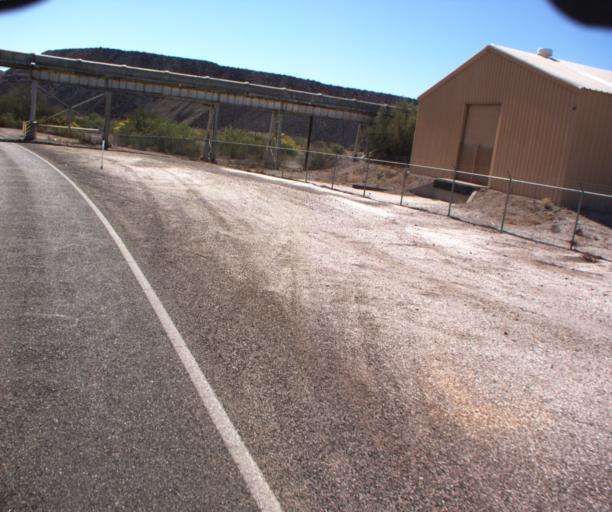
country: US
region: Arizona
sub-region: Pima County
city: Ajo
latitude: 32.3695
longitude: -112.8533
